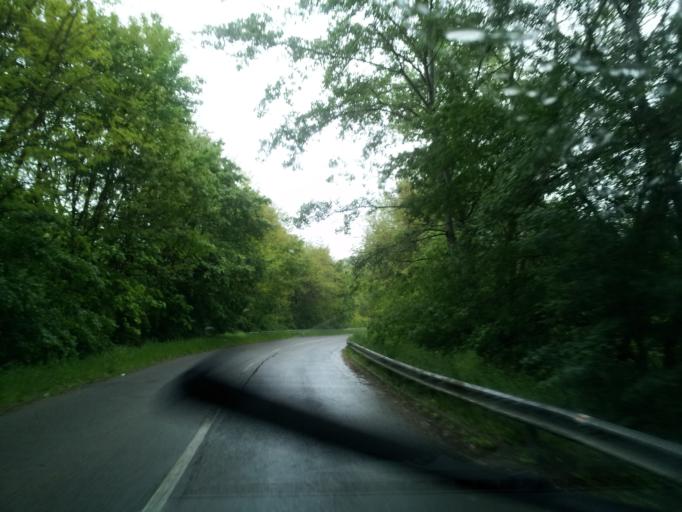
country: HU
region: Tolna
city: Bonyhad
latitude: 46.2631
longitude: 18.6097
